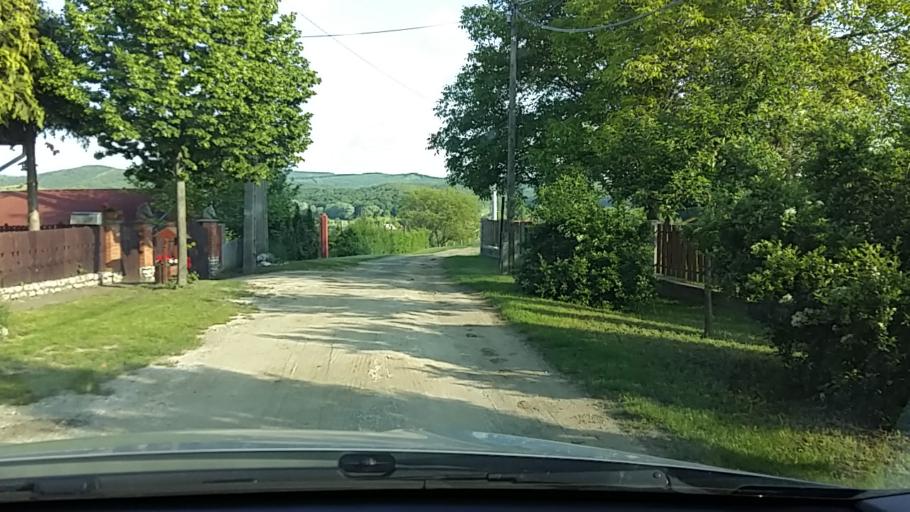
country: HU
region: Pest
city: Kosd
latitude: 47.8093
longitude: 19.2489
